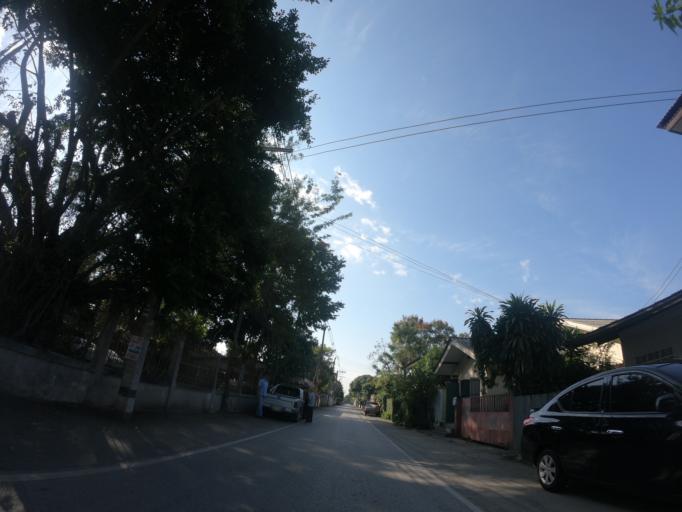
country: TH
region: Chiang Mai
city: Chiang Mai
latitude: 18.7811
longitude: 99.0352
